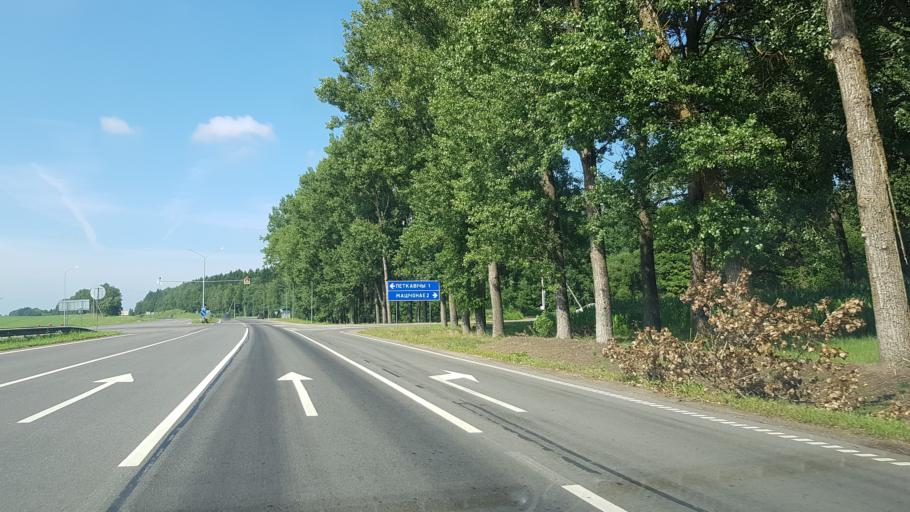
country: BY
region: Minsk
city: Dzyarzhynsk
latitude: 53.7030
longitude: 27.1950
